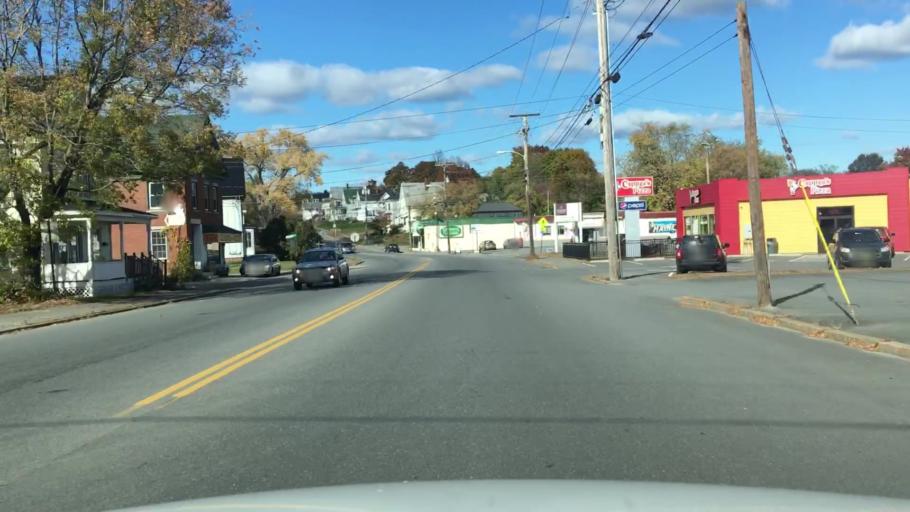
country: US
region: Maine
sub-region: Kennebec County
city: Waterville
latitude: 44.5571
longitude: -69.6322
